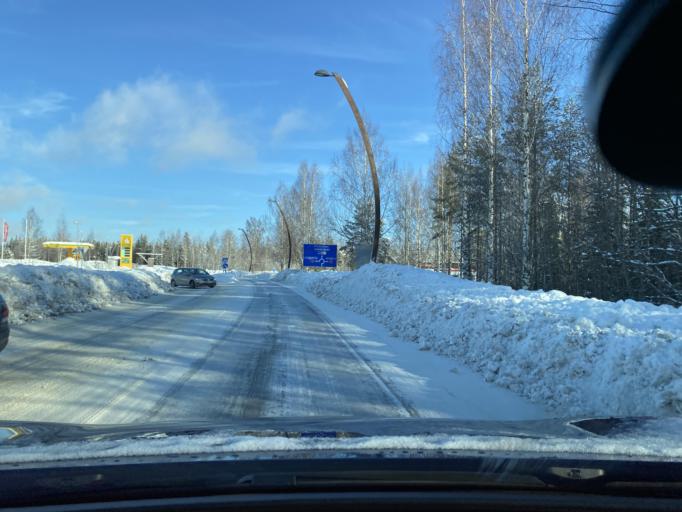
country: FI
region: Southern Savonia
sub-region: Mikkeli
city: Kangasniemi
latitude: 62.0014
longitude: 26.6553
